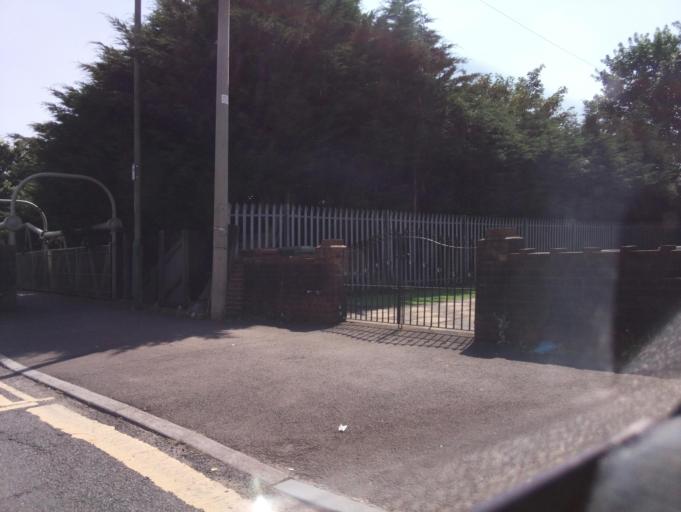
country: GB
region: Wales
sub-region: Caerphilly County Borough
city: Caerphilly
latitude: 51.5751
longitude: -3.2357
